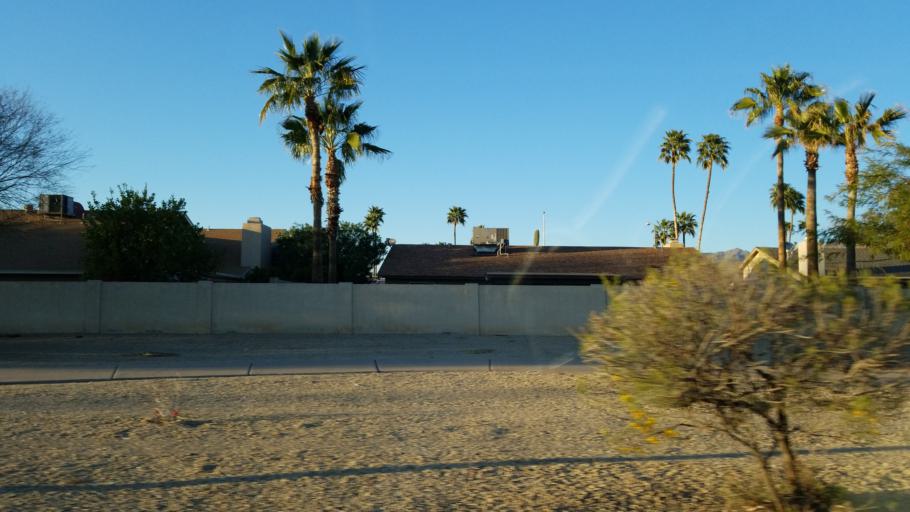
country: US
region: Arizona
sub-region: Maricopa County
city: Scottsdale
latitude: 33.5826
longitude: -111.8493
